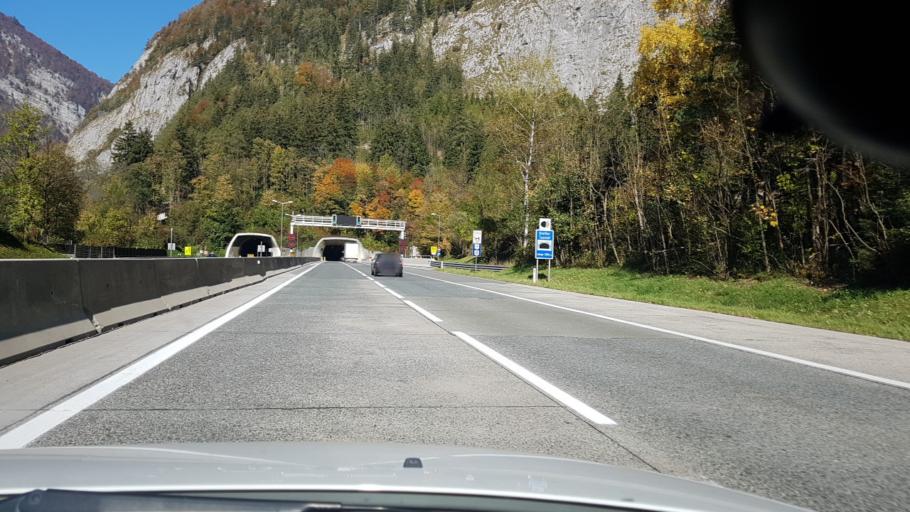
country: AT
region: Salzburg
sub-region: Politischer Bezirk Hallein
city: Golling an der Salzach
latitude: 47.5452
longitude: 13.1746
